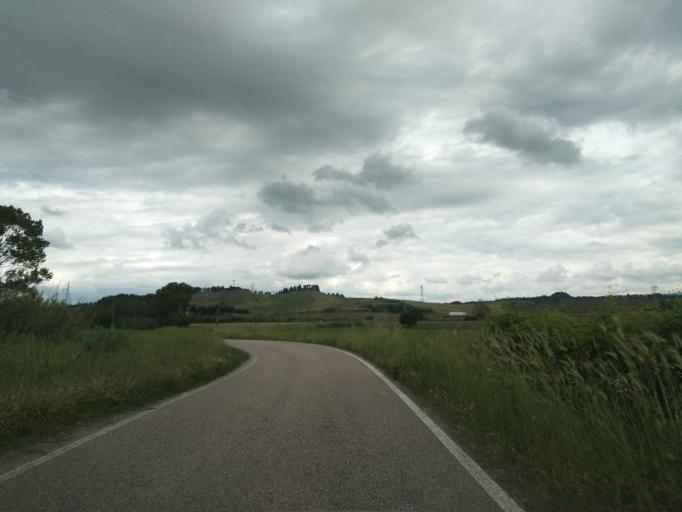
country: IT
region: Tuscany
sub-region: Provincia di Livorno
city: Collesalvetti
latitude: 43.5389
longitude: 10.4590
